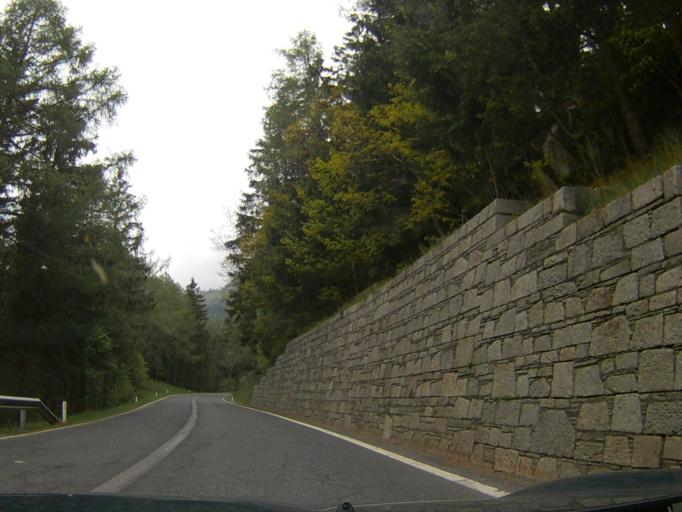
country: AT
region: Carinthia
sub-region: Politischer Bezirk Spittal an der Drau
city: Obervellach
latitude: 46.9417
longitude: 13.1907
